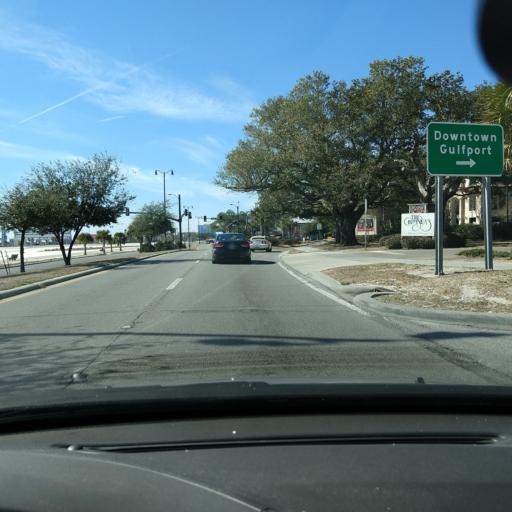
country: US
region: Mississippi
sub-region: Harrison County
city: Gulfport
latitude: 30.3696
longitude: -89.0813
